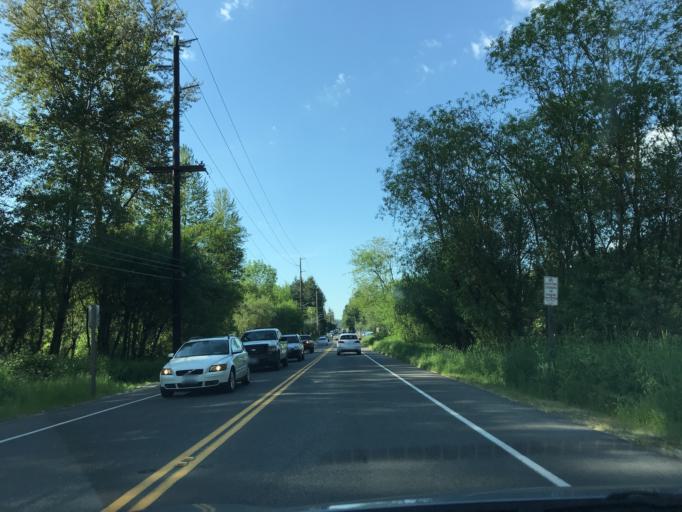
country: US
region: Washington
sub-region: King County
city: Issaquah
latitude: 47.4980
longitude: -122.0221
